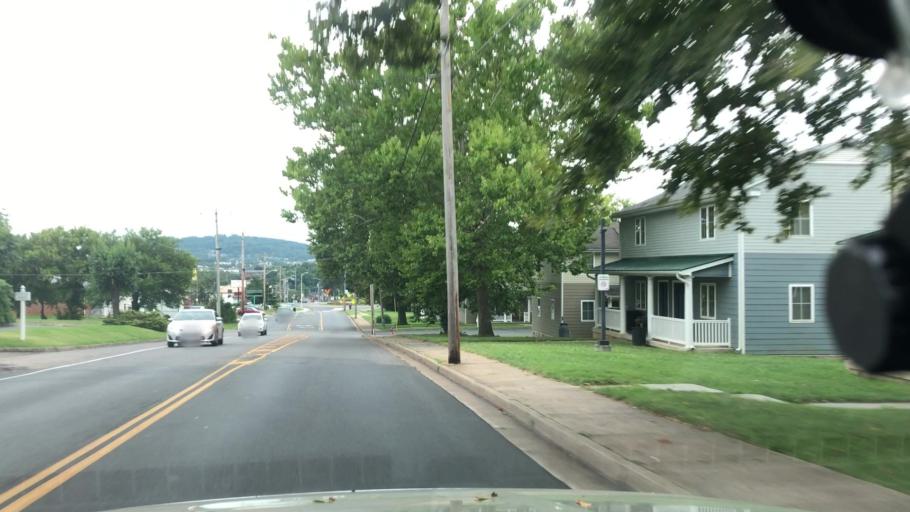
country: US
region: Virginia
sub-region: City of Harrisonburg
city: Harrisonburg
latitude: 38.4452
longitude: -78.8590
